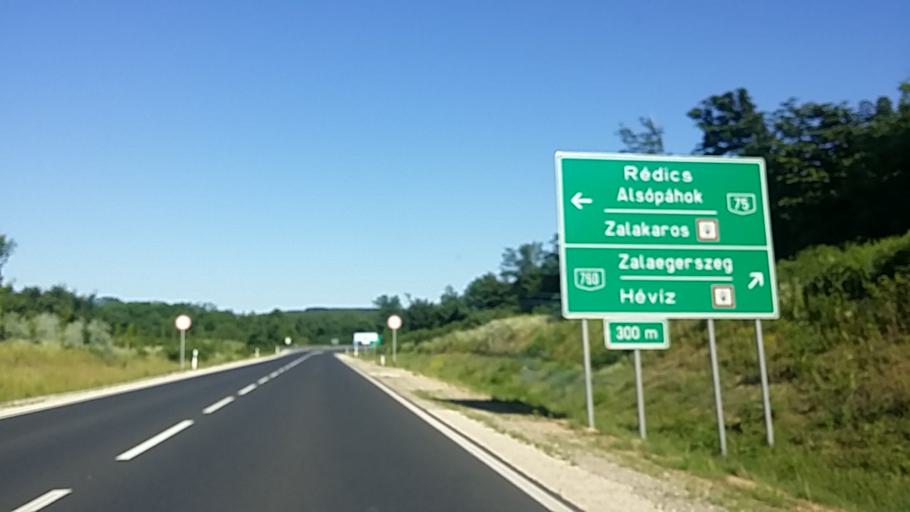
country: HU
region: Zala
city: Heviz
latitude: 46.7617
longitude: 17.1937
